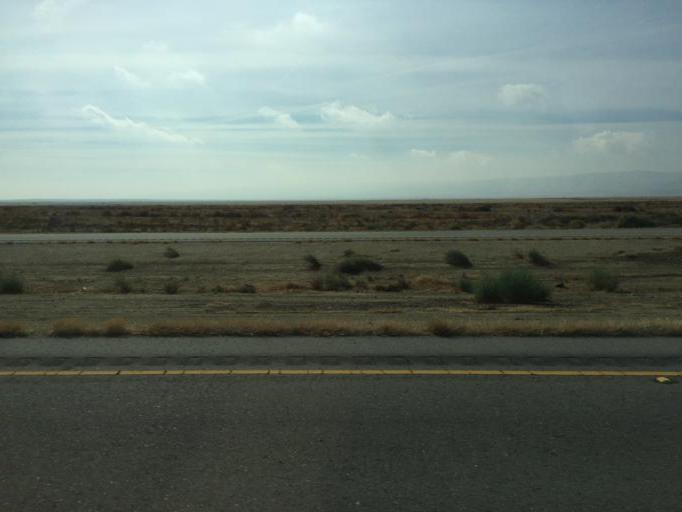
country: US
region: California
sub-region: Kern County
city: Lost Hills
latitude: 35.6148
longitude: -119.8982
